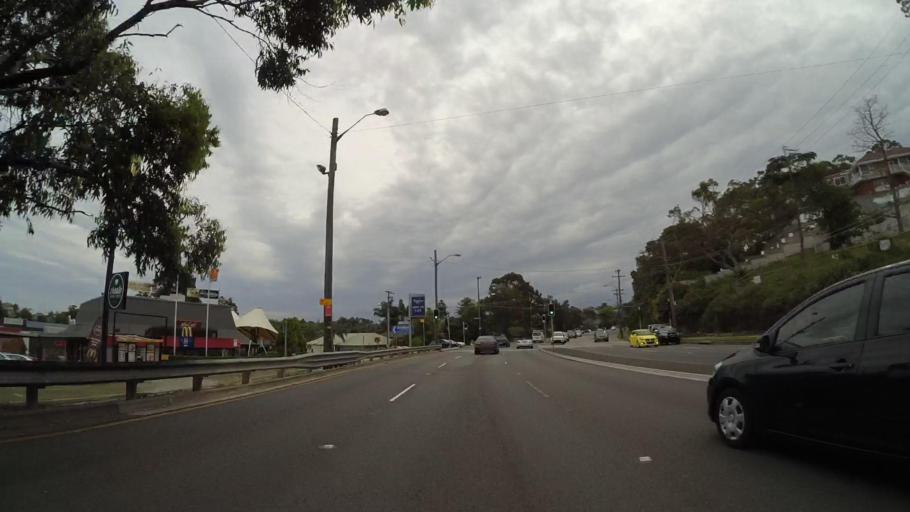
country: AU
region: New South Wales
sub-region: Kogarah
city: Blakehurst
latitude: -34.0086
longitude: 151.1037
